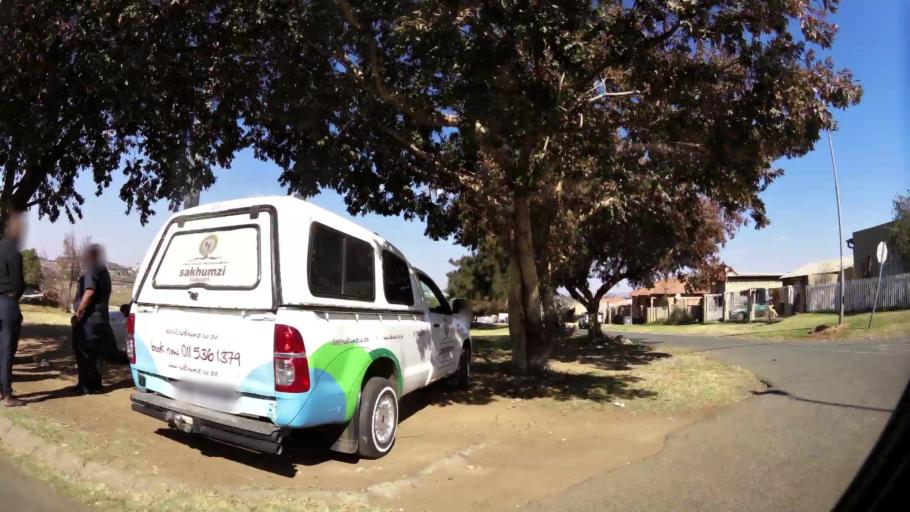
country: ZA
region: Gauteng
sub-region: City of Johannesburg Metropolitan Municipality
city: Soweto
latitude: -26.2432
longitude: 27.9044
